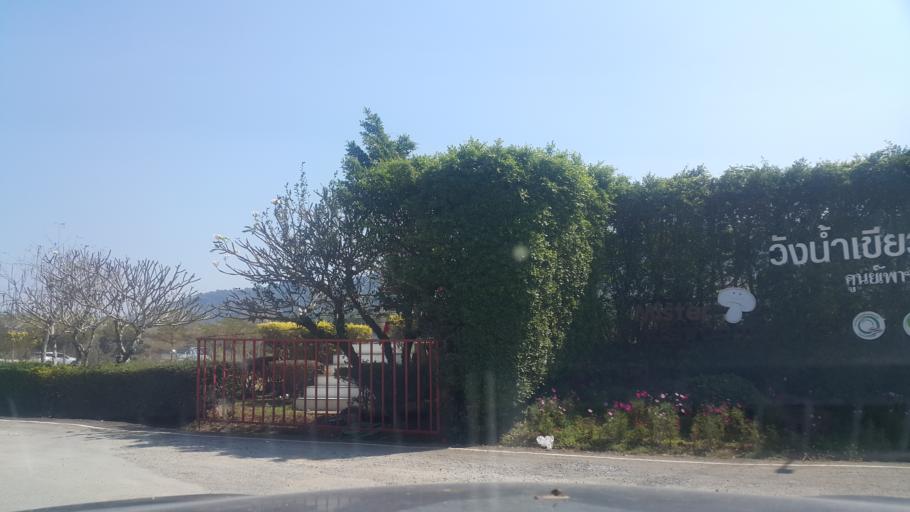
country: TH
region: Nakhon Ratchasima
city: Wang Nam Khiao
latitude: 14.3409
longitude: 101.9435
